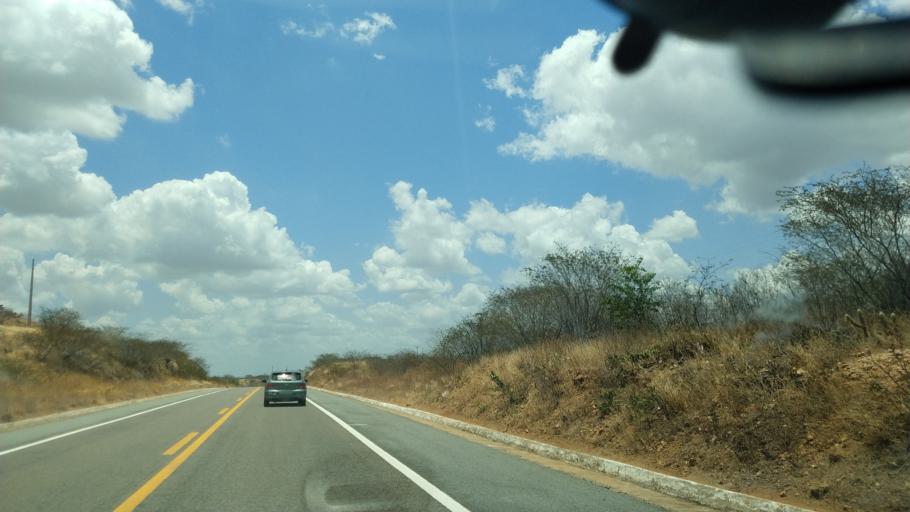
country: BR
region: Rio Grande do Norte
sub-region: Cerro Cora
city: Cerro Cora
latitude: -6.2086
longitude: -36.3124
